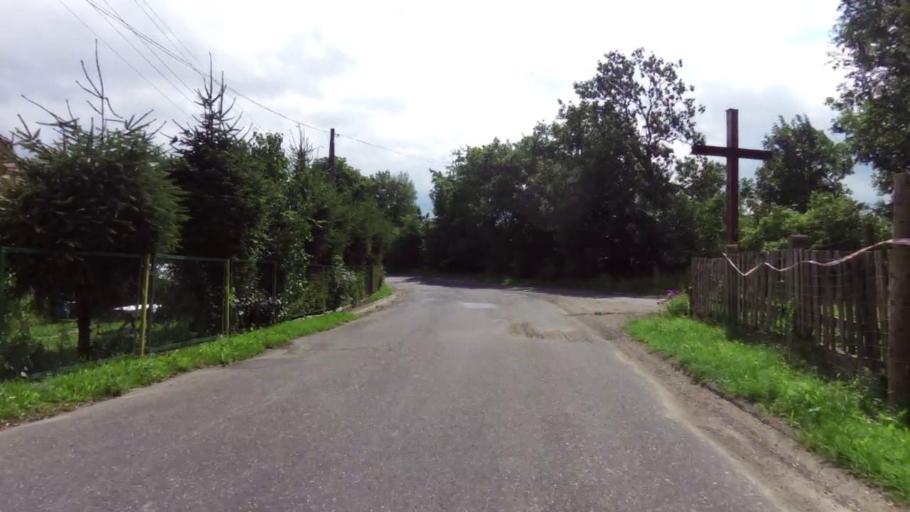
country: PL
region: West Pomeranian Voivodeship
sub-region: Powiat gryfinski
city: Cedynia
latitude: 52.8619
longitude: 14.2630
